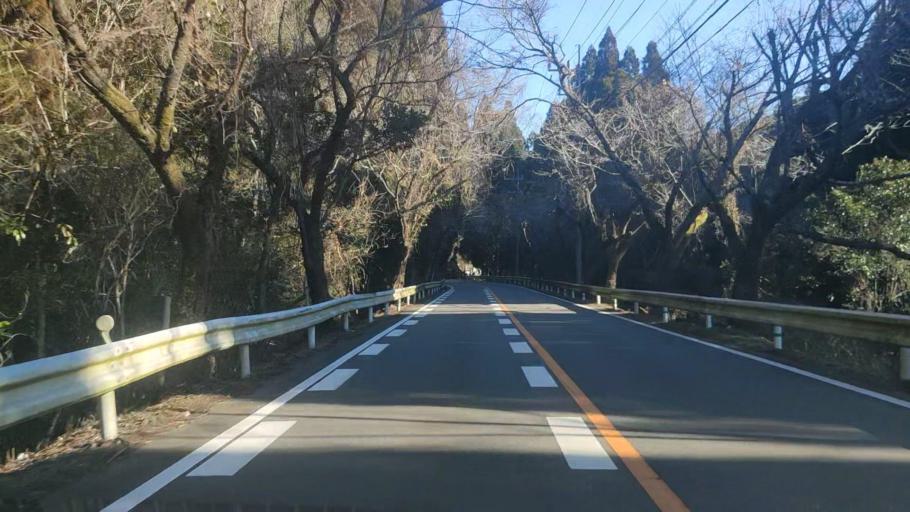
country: JP
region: Miyazaki
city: Nobeoka
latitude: 32.6395
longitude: 131.7434
